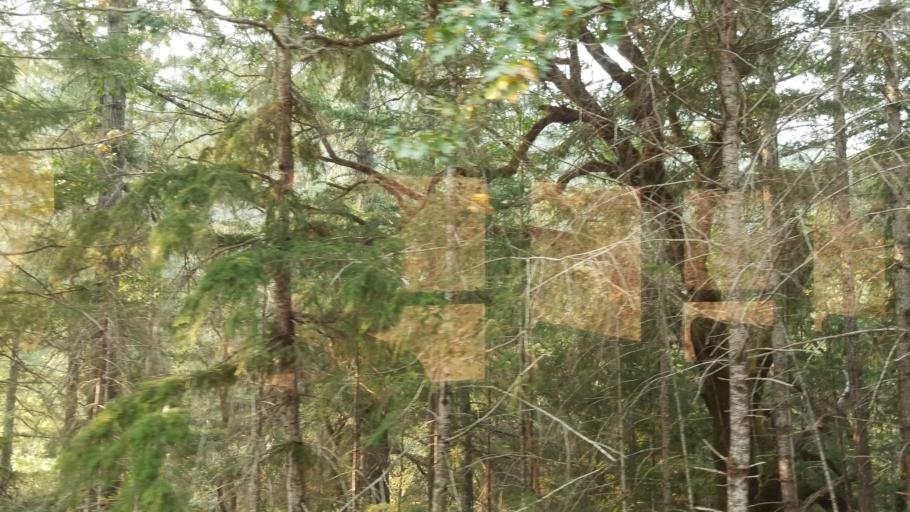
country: US
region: California
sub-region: Mendocino County
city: Willits
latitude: 39.4031
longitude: -123.3965
